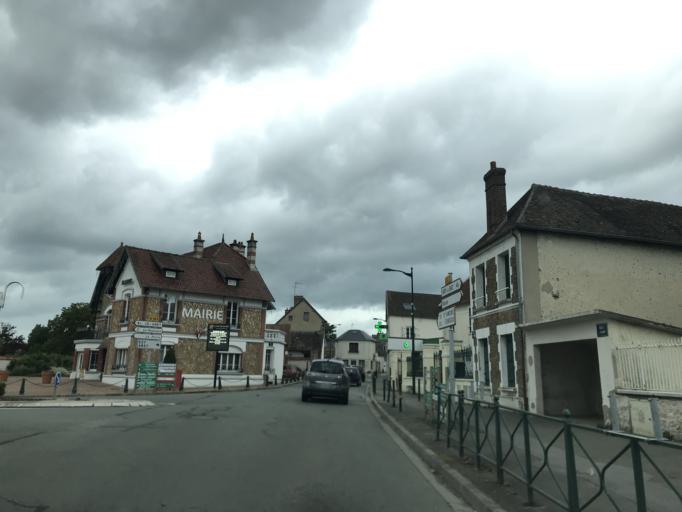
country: FR
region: Haute-Normandie
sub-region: Departement de l'Eure
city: La Couture-Boussey
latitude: 48.8979
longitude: 1.4068
